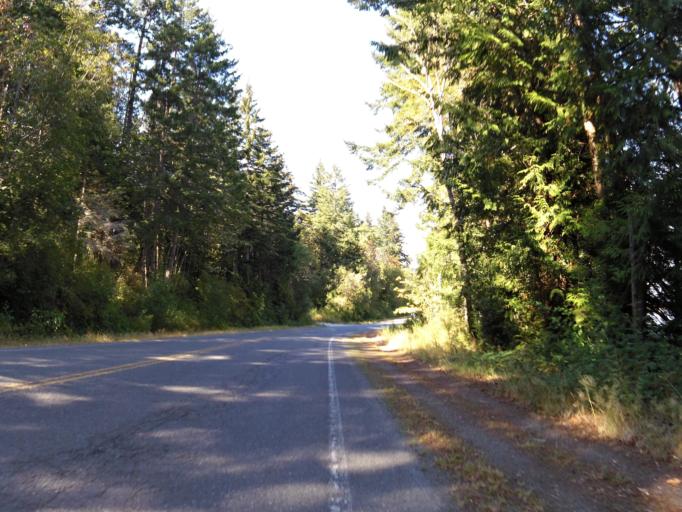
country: CA
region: British Columbia
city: North Saanich
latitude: 48.6300
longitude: -123.5302
